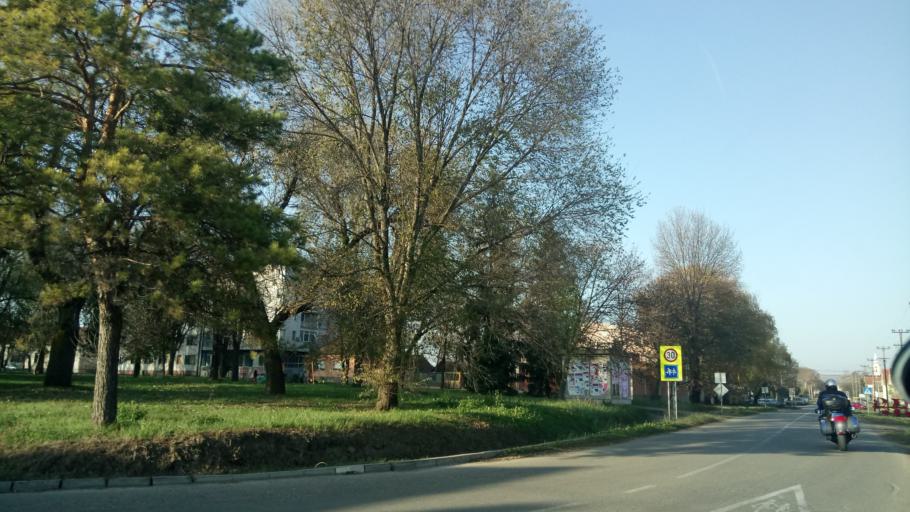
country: RS
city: Beska
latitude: 45.1247
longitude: 20.0674
